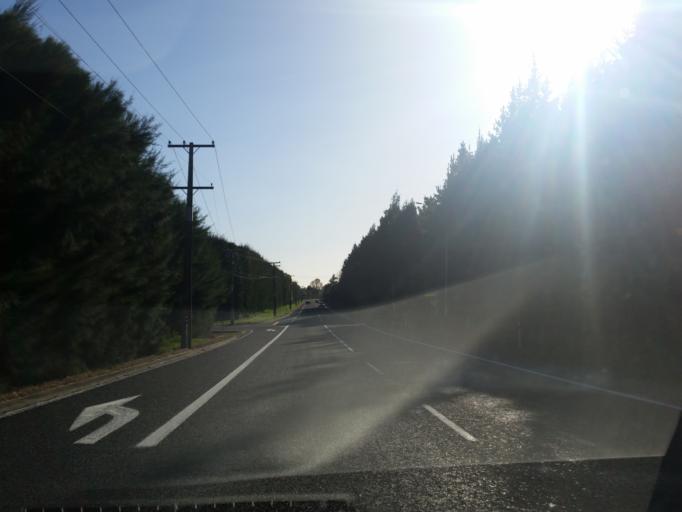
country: NZ
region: Bay of Plenty
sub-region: Western Bay of Plenty District
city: Katikati
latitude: -37.5124
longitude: 175.9196
